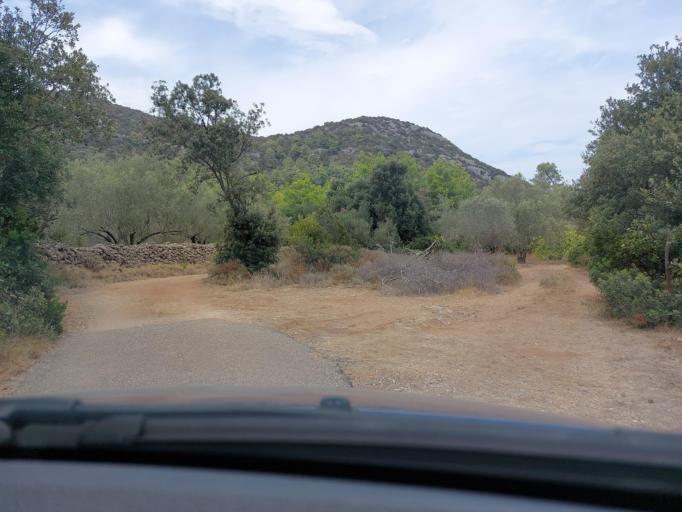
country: HR
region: Dubrovacko-Neretvanska
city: Smokvica
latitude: 42.7609
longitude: 16.9344
